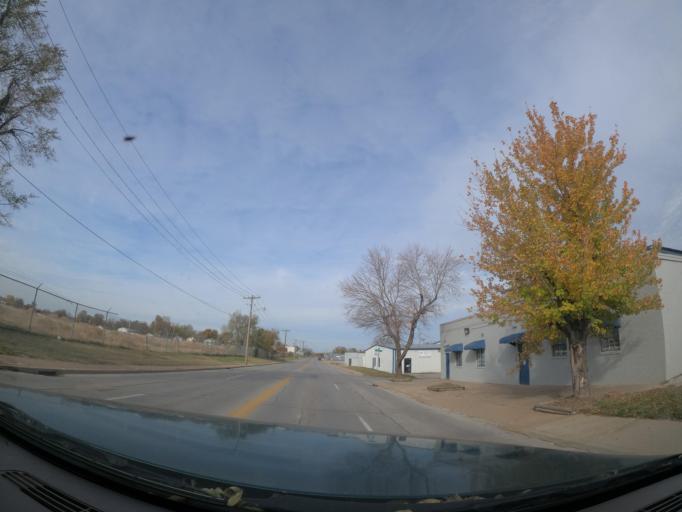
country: US
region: Oklahoma
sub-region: Tulsa County
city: Tulsa
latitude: 36.1701
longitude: -95.9671
